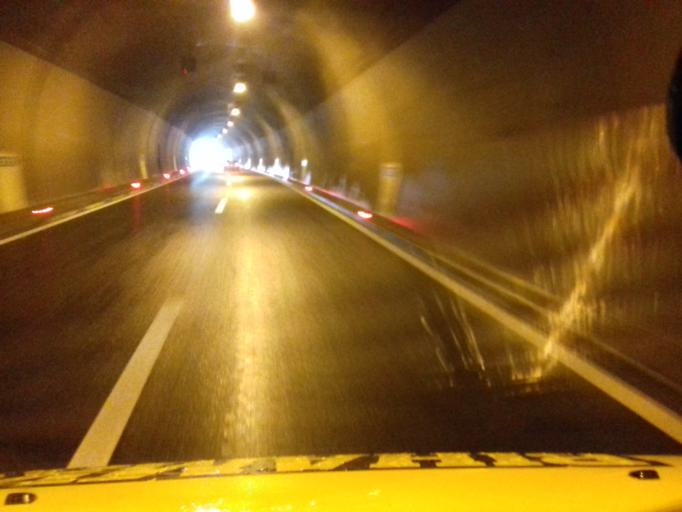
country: BA
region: Federation of Bosnia and Herzegovina
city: Vogosca
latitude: 43.8886
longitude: 18.3144
